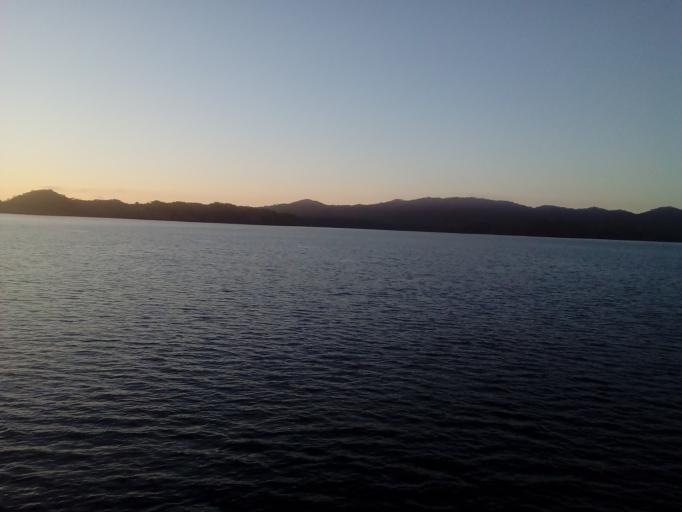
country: CR
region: Puntarenas
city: Paquera
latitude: 9.8652
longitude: -84.8888
